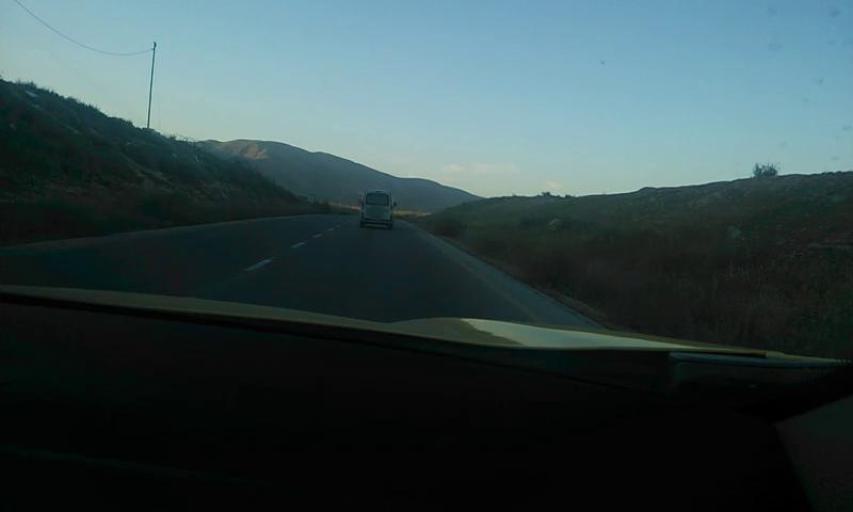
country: PS
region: West Bank
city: An Nuway`imah
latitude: 31.9125
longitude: 35.4218
